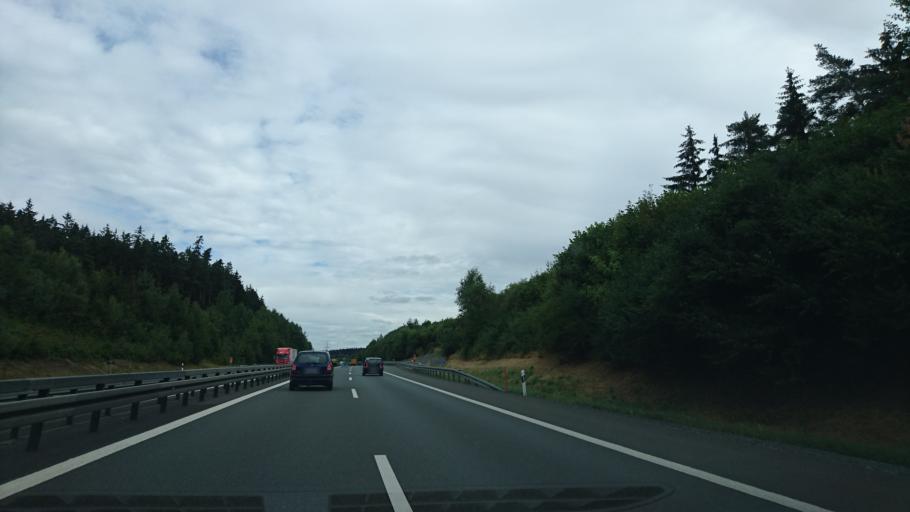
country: DE
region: Bavaria
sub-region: Upper Franconia
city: Thiersheim
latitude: 50.0465
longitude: 12.1037
